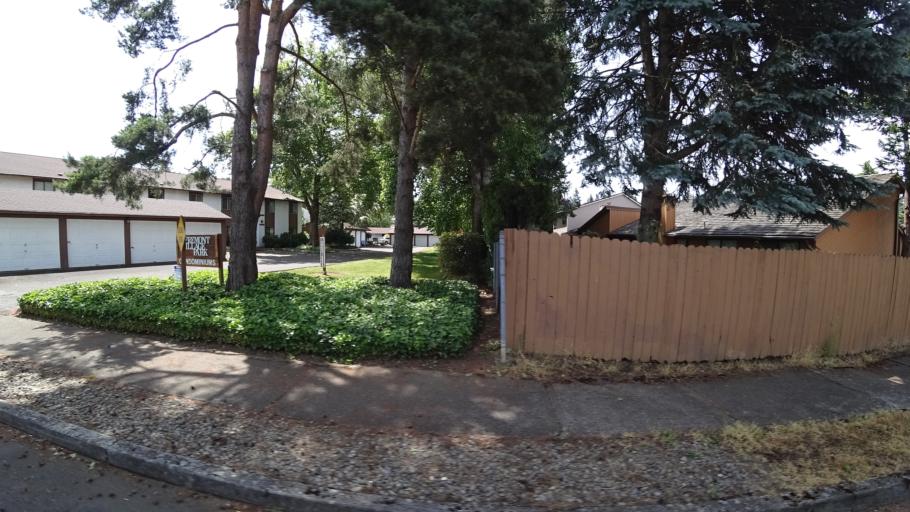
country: US
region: Oregon
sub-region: Multnomah County
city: Fairview
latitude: 45.5481
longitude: -122.4993
